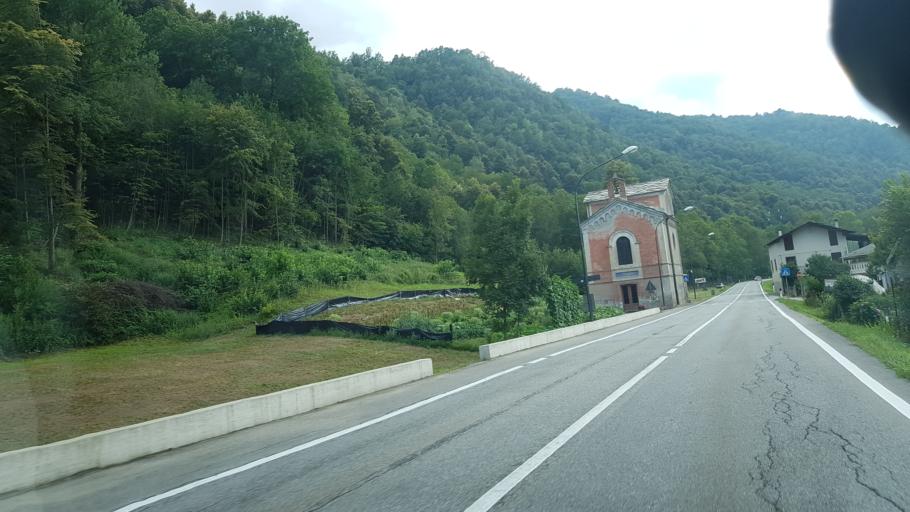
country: IT
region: Piedmont
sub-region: Provincia di Cuneo
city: Melle
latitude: 44.5616
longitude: 7.3163
